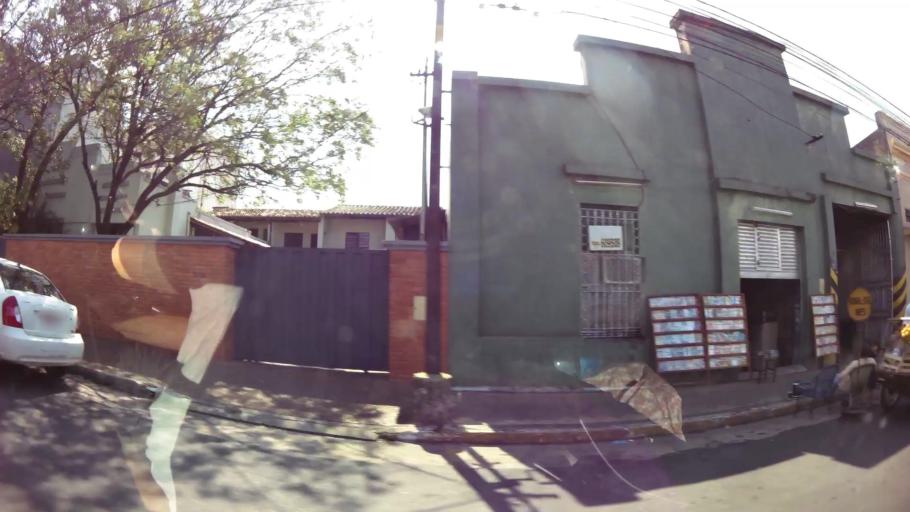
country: PY
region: Asuncion
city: Asuncion
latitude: -25.2873
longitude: -57.6379
